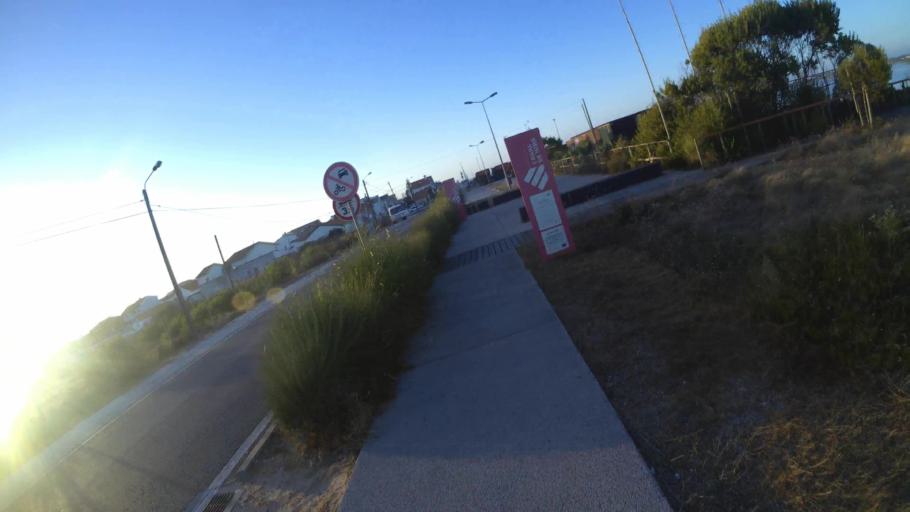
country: PT
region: Aveiro
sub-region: Ilhavo
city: Gafanha da Encarnacao
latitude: 40.6065
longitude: -8.7488
